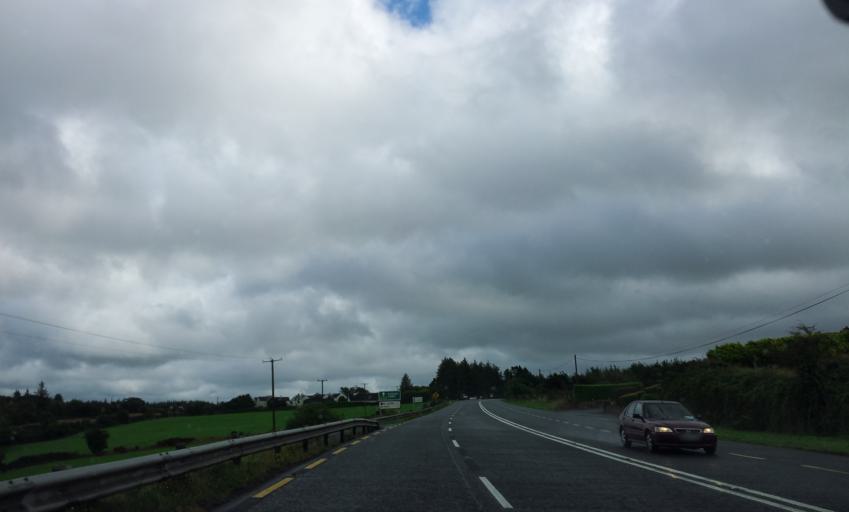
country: IE
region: Munster
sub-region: Waterford
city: Dungarvan
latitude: 52.0500
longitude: -7.6608
